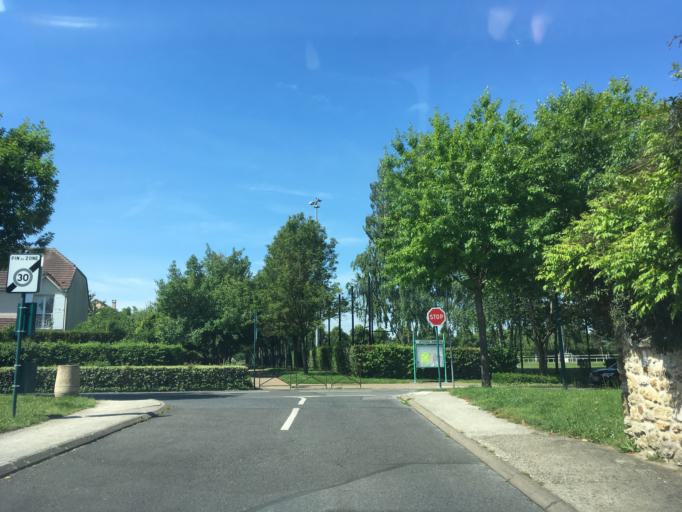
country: FR
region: Ile-de-France
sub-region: Departement de Seine-et-Marne
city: Magny-le-Hongre
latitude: 48.8619
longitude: 2.8111
